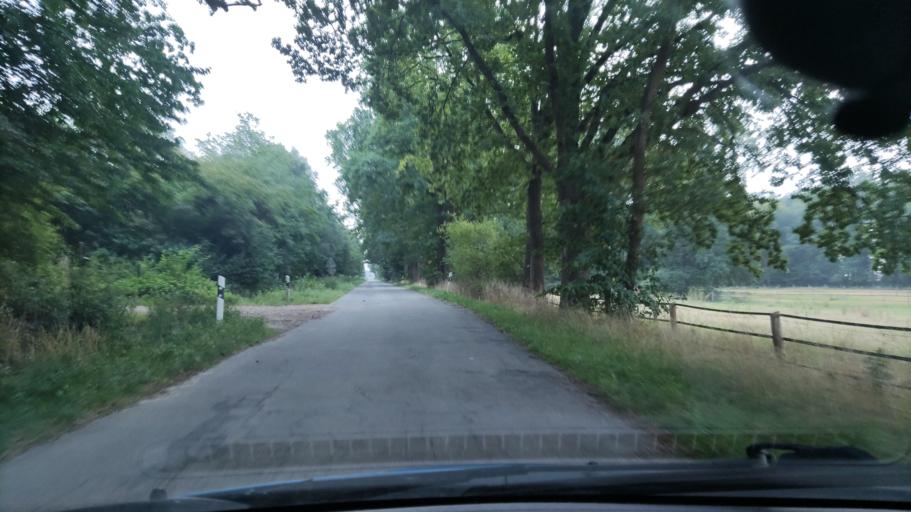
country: DE
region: Lower Saxony
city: Altenmedingen
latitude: 53.1437
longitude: 10.5866
